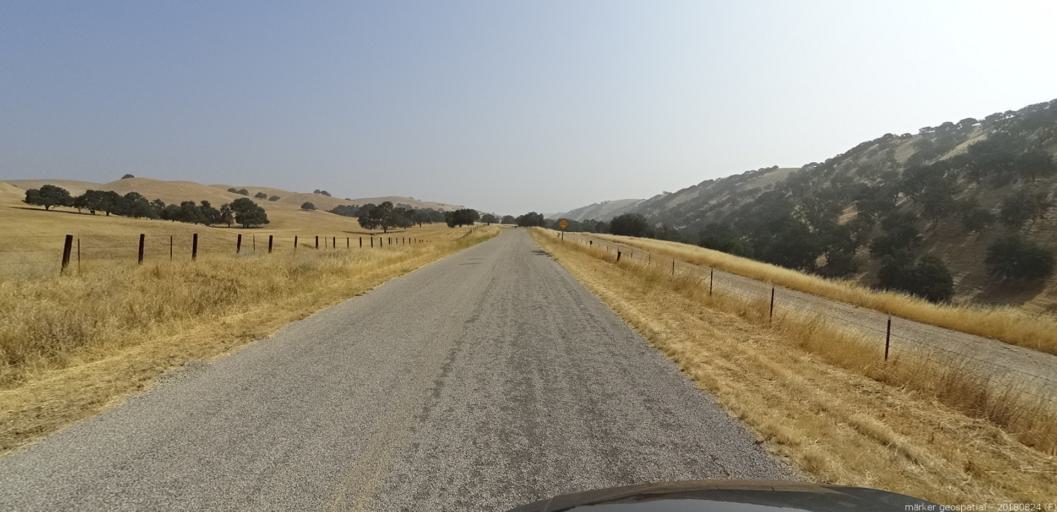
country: US
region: California
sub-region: San Luis Obispo County
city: San Miguel
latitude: 35.8641
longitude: -120.7633
